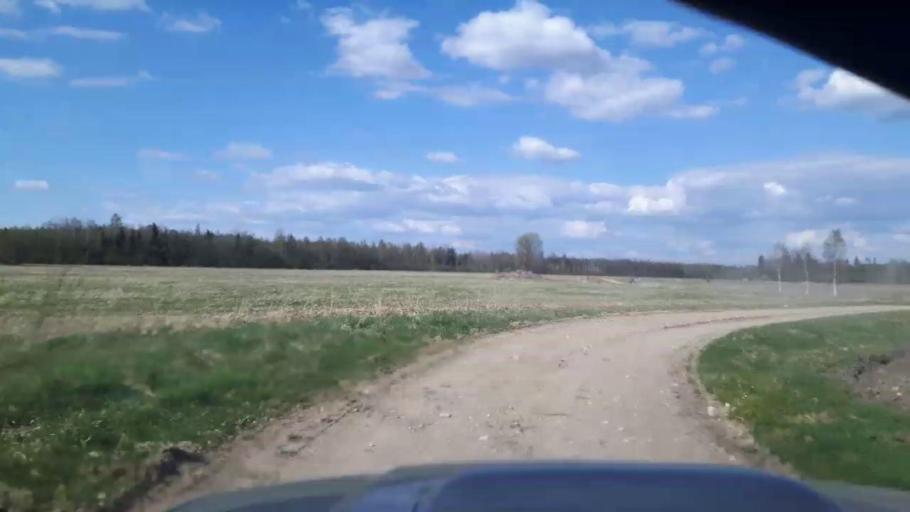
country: EE
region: Paernumaa
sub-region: Tootsi vald
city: Tootsi
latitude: 58.4384
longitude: 24.8732
